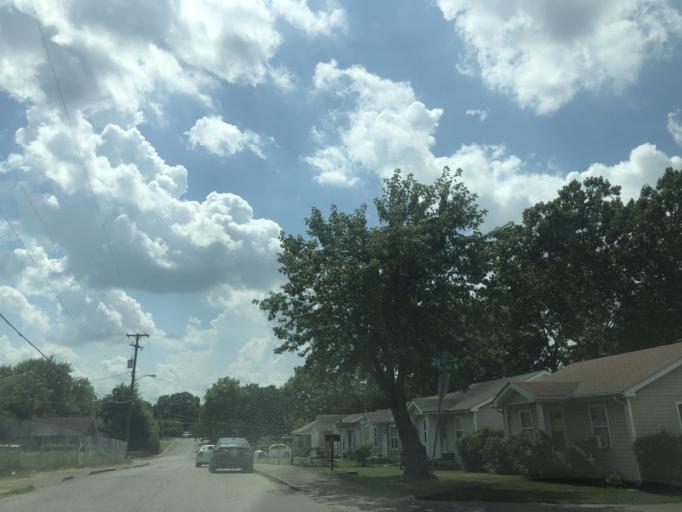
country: US
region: Tennessee
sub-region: Davidson County
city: Nashville
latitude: 36.1608
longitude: -86.8159
